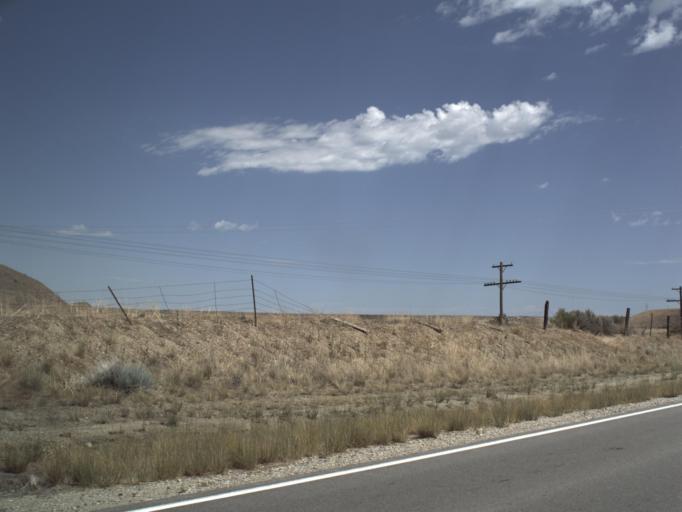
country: US
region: Utah
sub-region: Tooele County
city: Tooele
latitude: 40.4367
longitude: -112.3735
